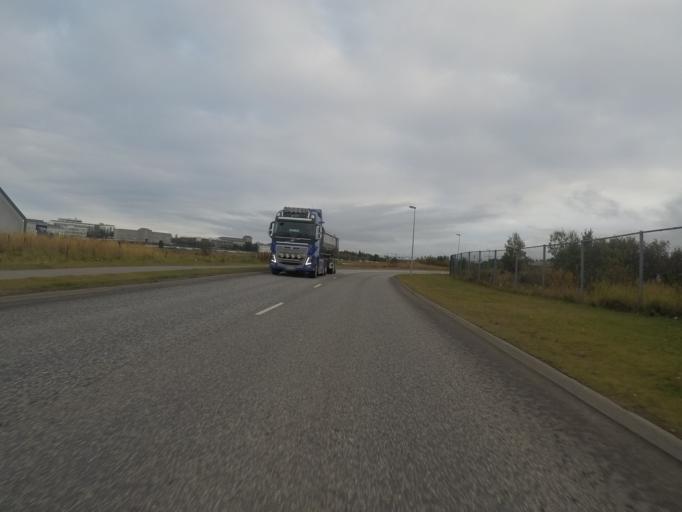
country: IS
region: Capital Region
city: Kopavogur
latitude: 64.1367
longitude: -21.9429
